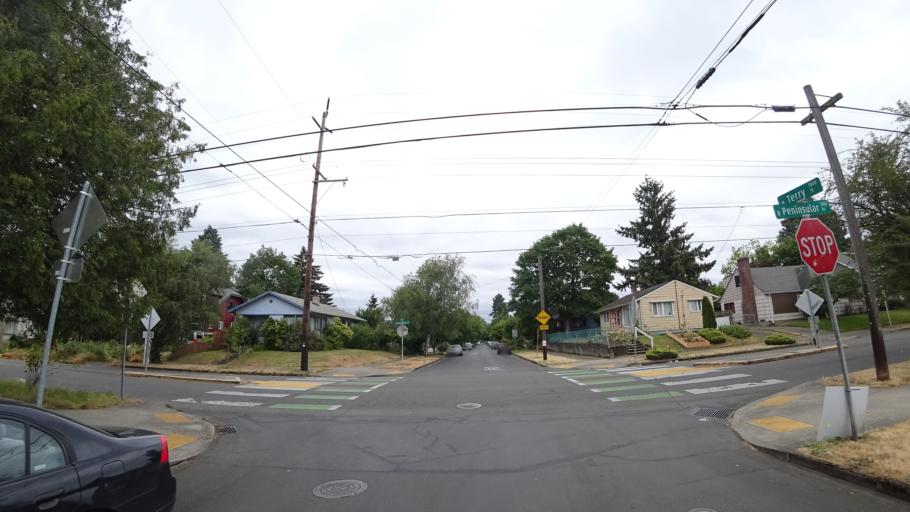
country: US
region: Oregon
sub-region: Multnomah County
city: Portland
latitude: 45.5799
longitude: -122.6975
